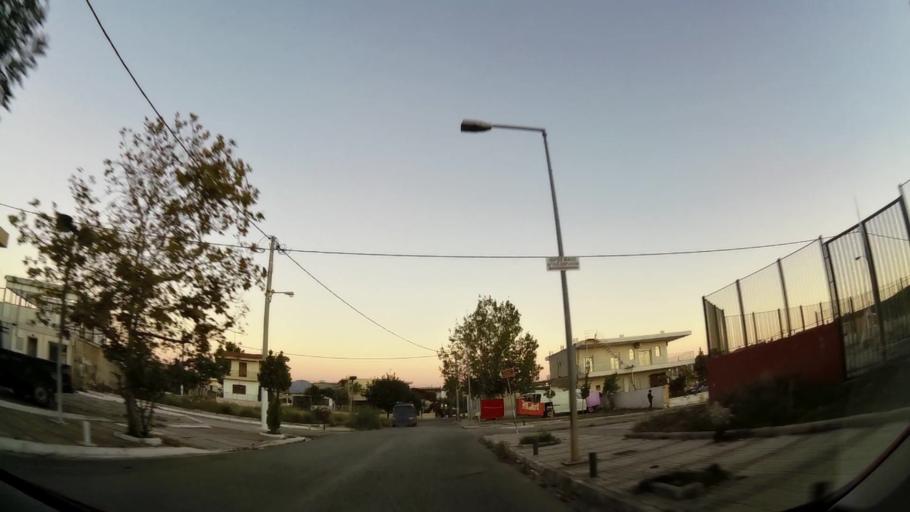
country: GR
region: Attica
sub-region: Nomarchia Dytikis Attikis
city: Ano Liosia
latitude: 38.0820
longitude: 23.6923
